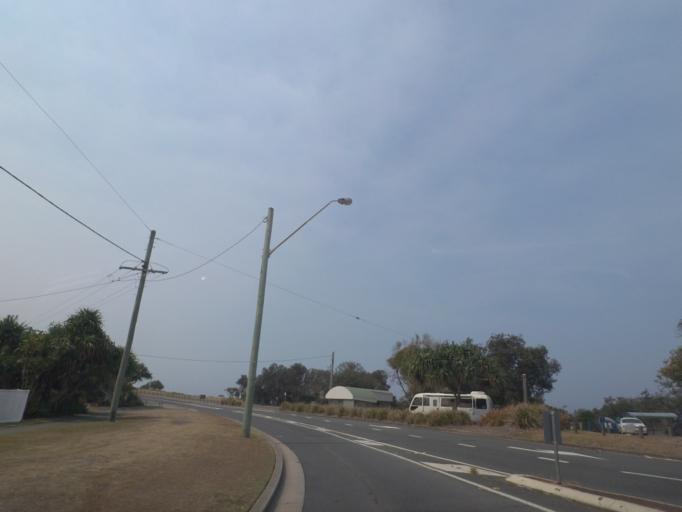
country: AU
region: New South Wales
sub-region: Tweed
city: Casuarina
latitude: -28.3364
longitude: 153.5742
